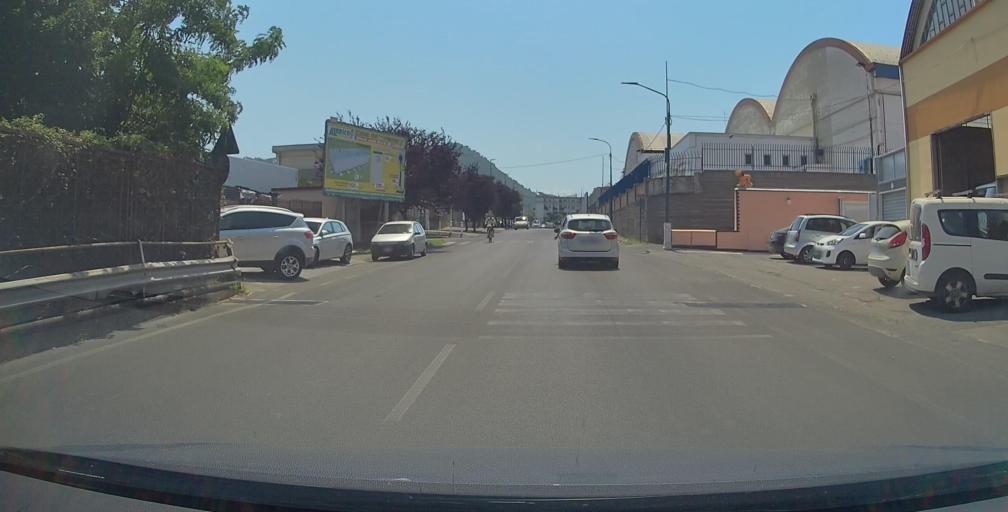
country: IT
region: Campania
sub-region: Provincia di Salerno
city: Cava De Tirreni
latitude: 40.7146
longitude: 14.6974
